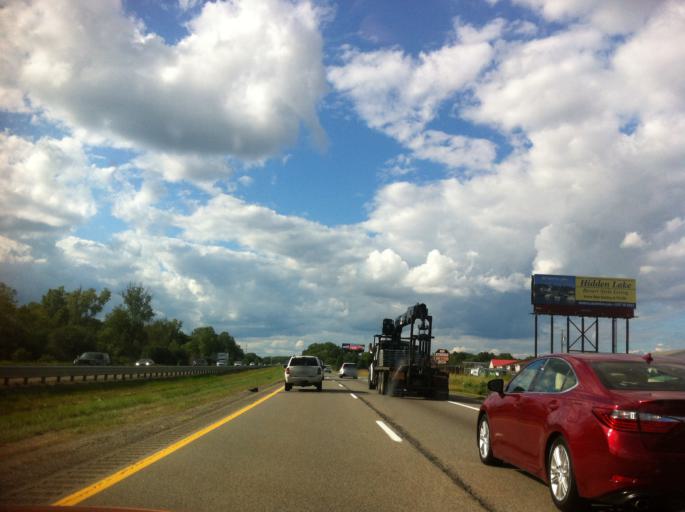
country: US
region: Michigan
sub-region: Livingston County
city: Whitmore Lake
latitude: 42.4100
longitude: -83.7632
